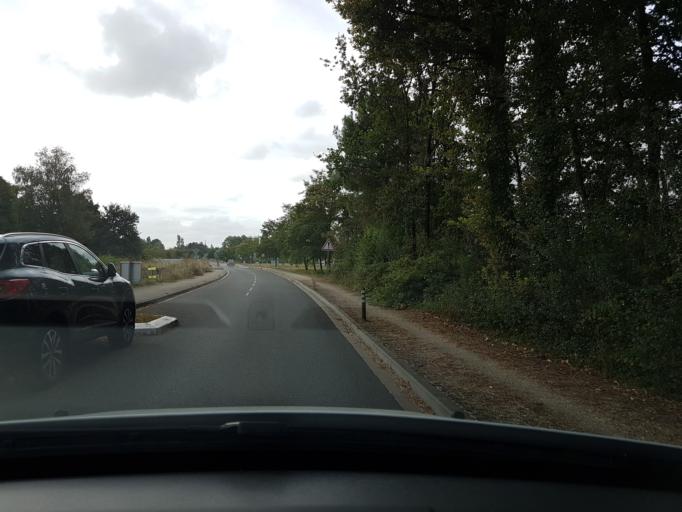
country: FR
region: Centre
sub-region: Departement d'Indre-et-Loire
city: Larcay
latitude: 47.3508
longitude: 0.7706
